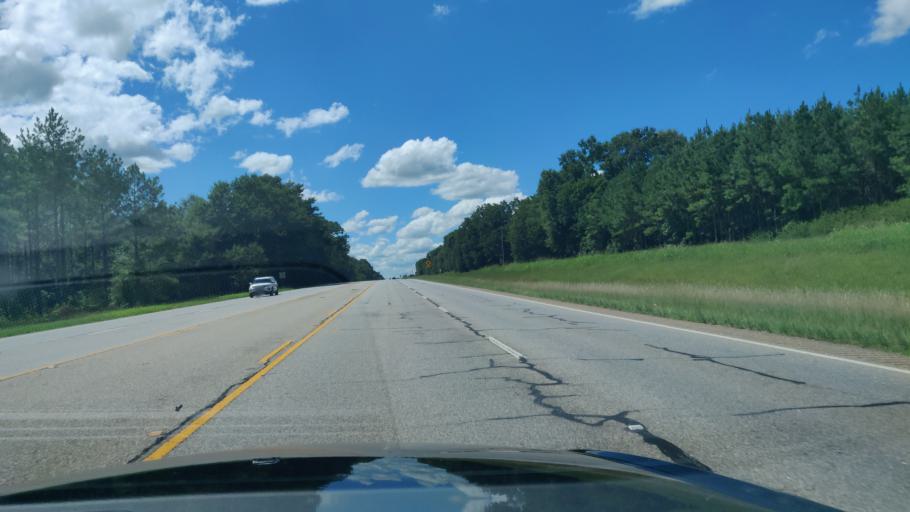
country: US
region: Georgia
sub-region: Webster County
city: Preston
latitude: 31.9783
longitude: -84.6179
